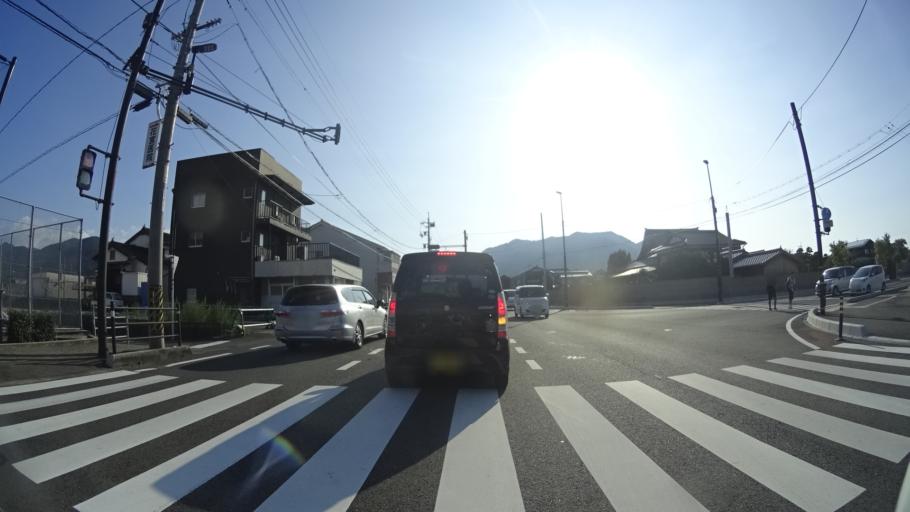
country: JP
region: Yamaguchi
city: Hagi
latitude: 34.4075
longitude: 131.3920
